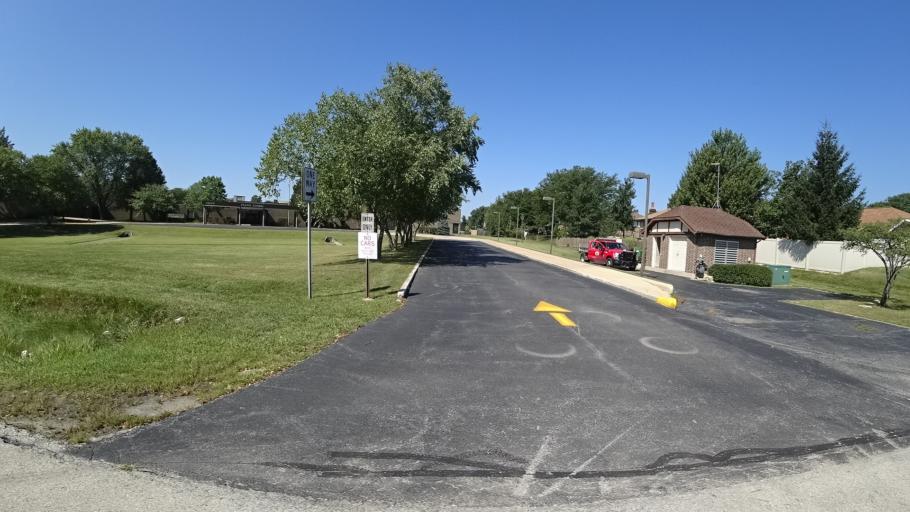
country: US
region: Illinois
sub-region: Cook County
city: Orland Park
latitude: 41.6340
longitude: -87.8198
